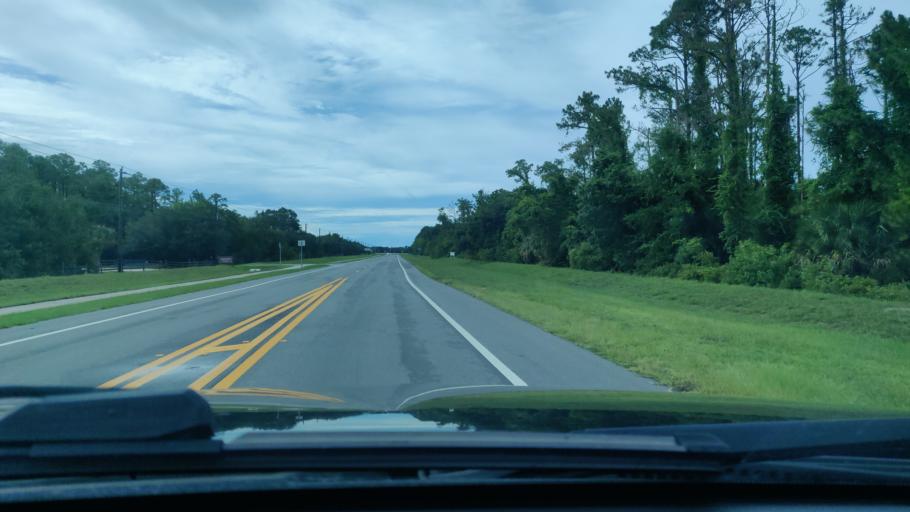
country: US
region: Florida
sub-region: Flagler County
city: Flagler Beach
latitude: 29.5075
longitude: -81.1608
